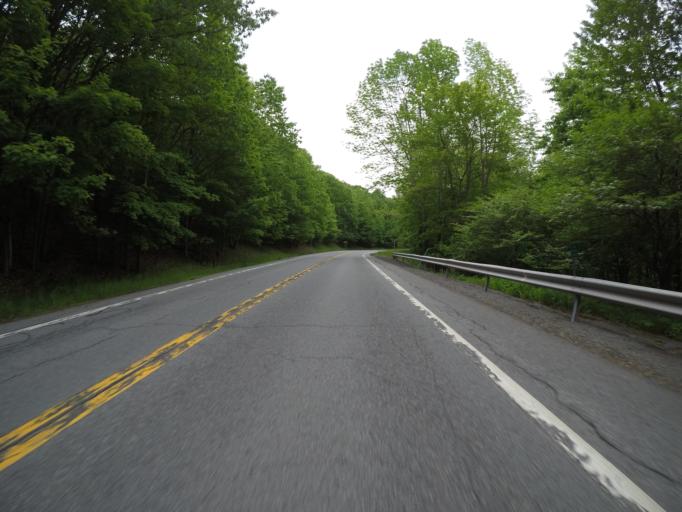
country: US
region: New York
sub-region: Sullivan County
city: Livingston Manor
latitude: 42.0697
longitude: -74.8795
